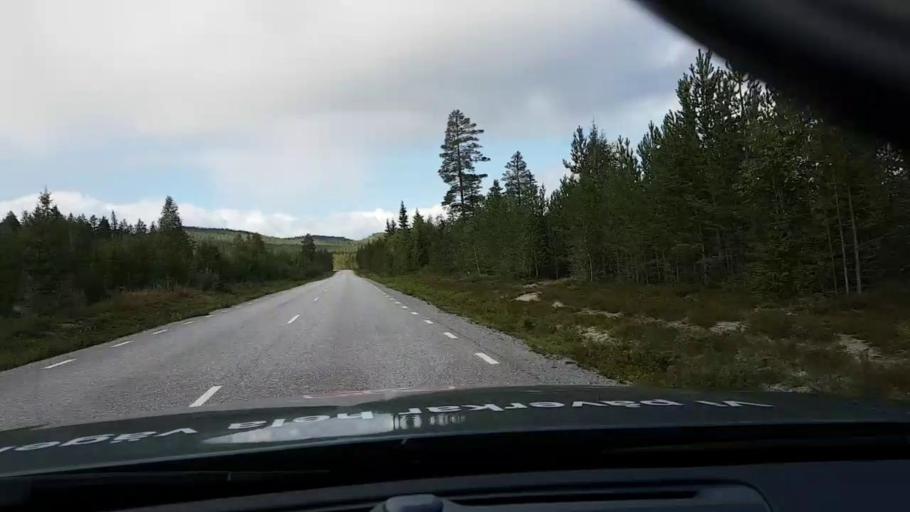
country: SE
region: Vaesternorrland
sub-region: OErnskoeldsviks Kommun
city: Bredbyn
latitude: 63.6806
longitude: 17.7849
